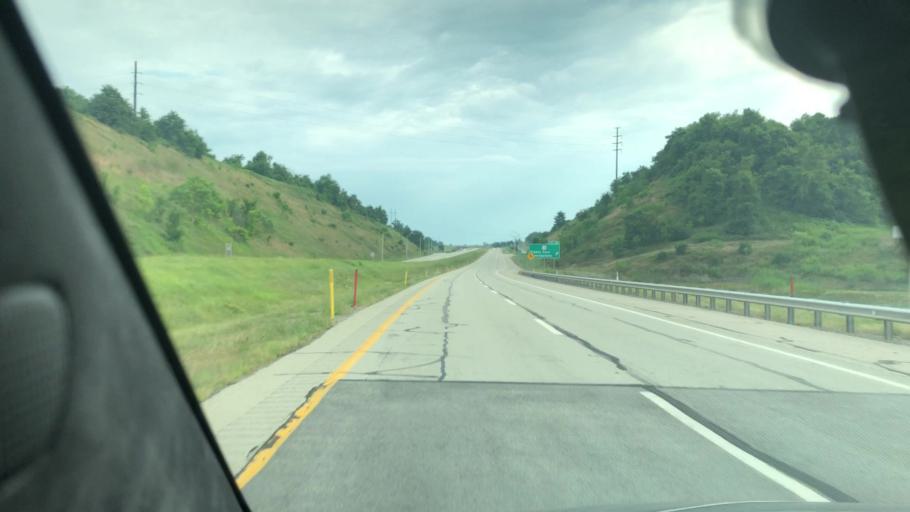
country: US
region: Pennsylvania
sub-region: Washington County
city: Baidland
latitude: 40.2053
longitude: -79.9852
